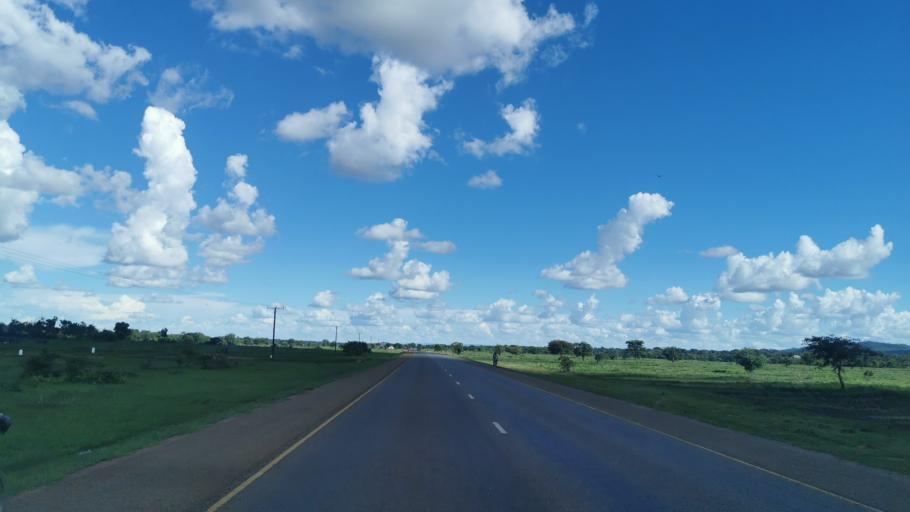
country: TZ
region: Geita
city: Ushirombo
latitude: -3.4782
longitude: 31.9181
